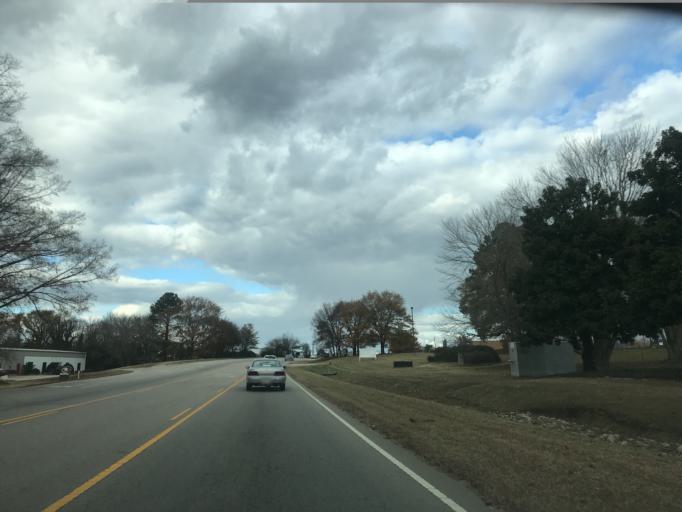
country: US
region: North Carolina
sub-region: Wake County
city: Raleigh
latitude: 35.7955
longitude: -78.5626
